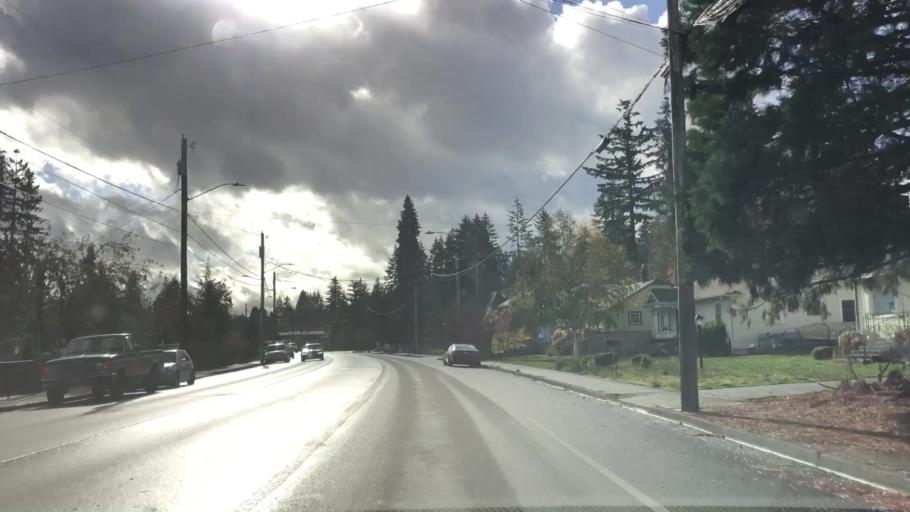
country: US
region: Washington
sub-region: Snohomish County
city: Everett
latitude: 47.9352
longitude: -122.2116
